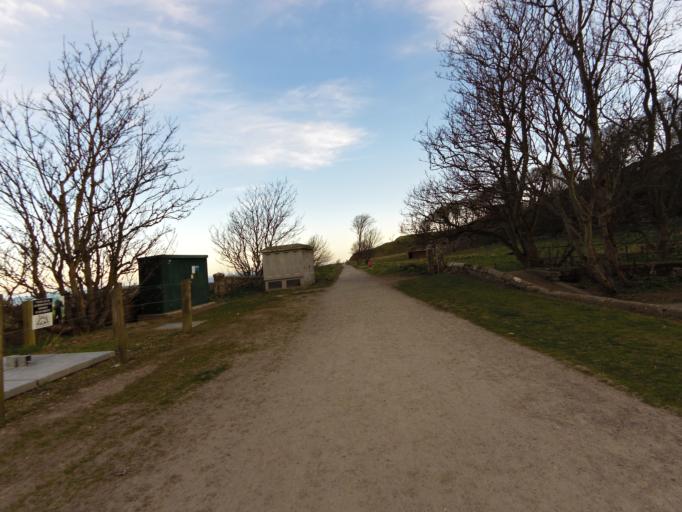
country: GB
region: Scotland
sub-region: Aberdeenshire
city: Inverbervie
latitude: 56.8399
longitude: -2.2761
